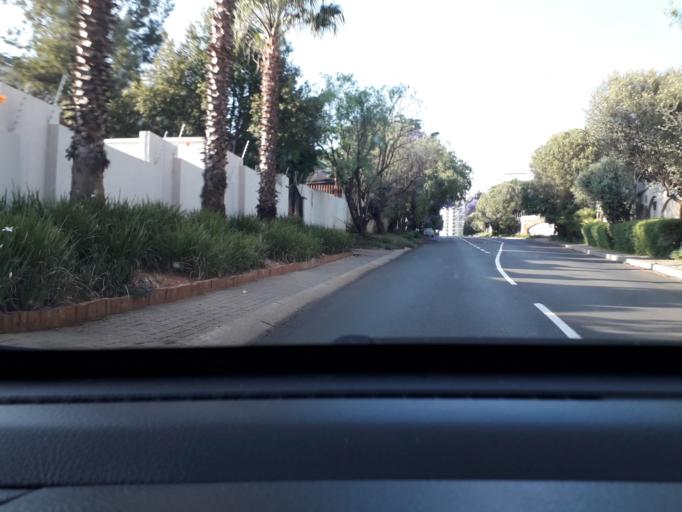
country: ZA
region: Gauteng
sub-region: City of Johannesburg Metropolitan Municipality
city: Modderfontein
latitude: -26.0894
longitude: 28.0551
